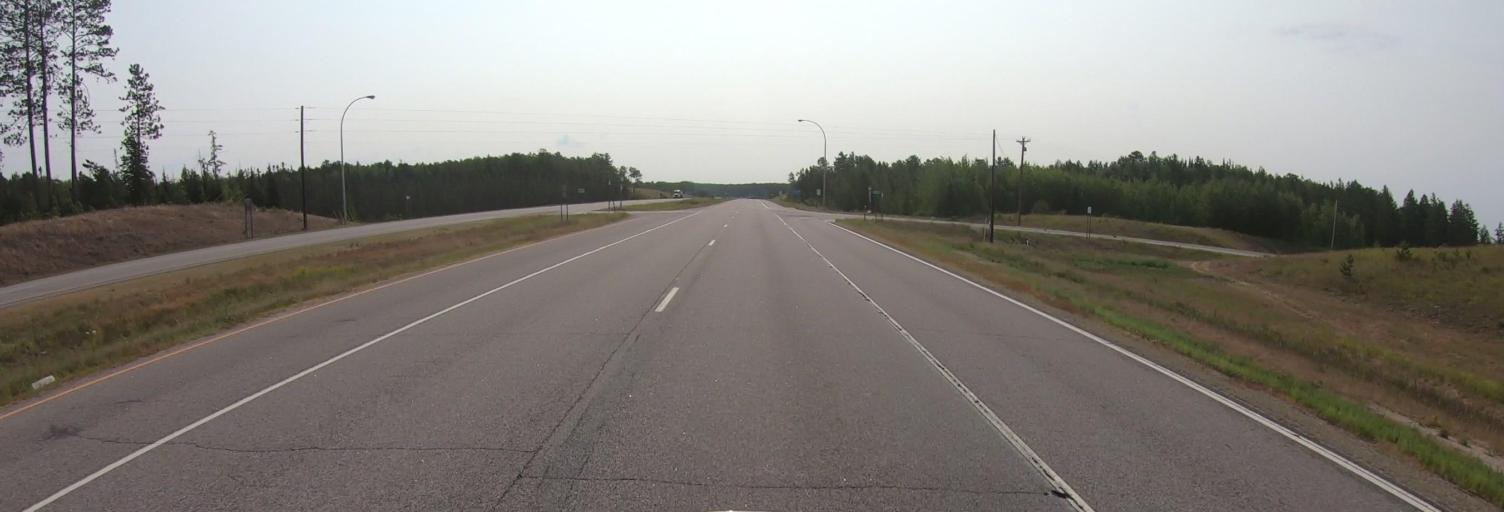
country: US
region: Minnesota
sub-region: Saint Louis County
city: Mountain Iron
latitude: 47.6648
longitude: -92.6358
